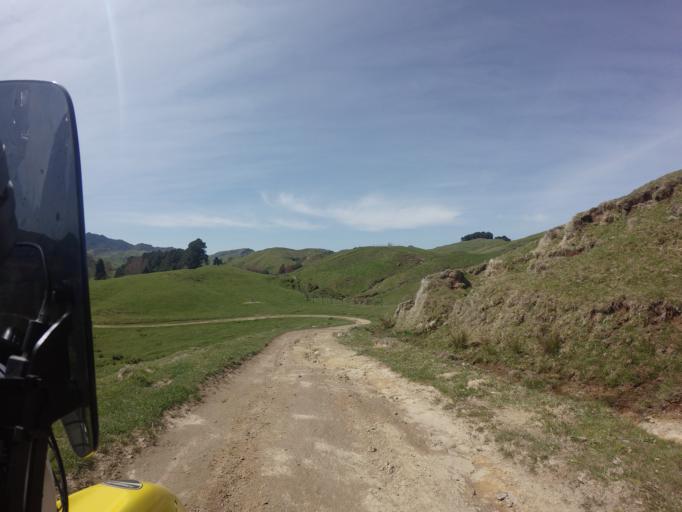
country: NZ
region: Bay of Plenty
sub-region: Opotiki District
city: Opotiki
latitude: -38.4652
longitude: 177.3799
